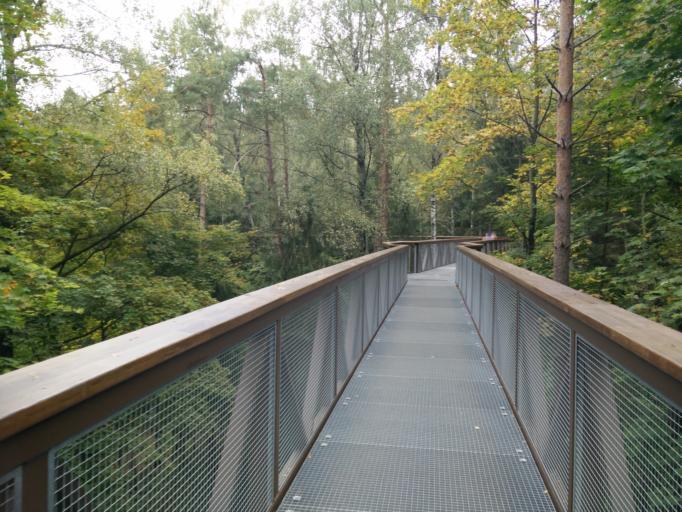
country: LT
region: Utenos apskritis
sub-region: Anyksciai
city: Anyksciai
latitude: 55.4850
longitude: 25.0619
